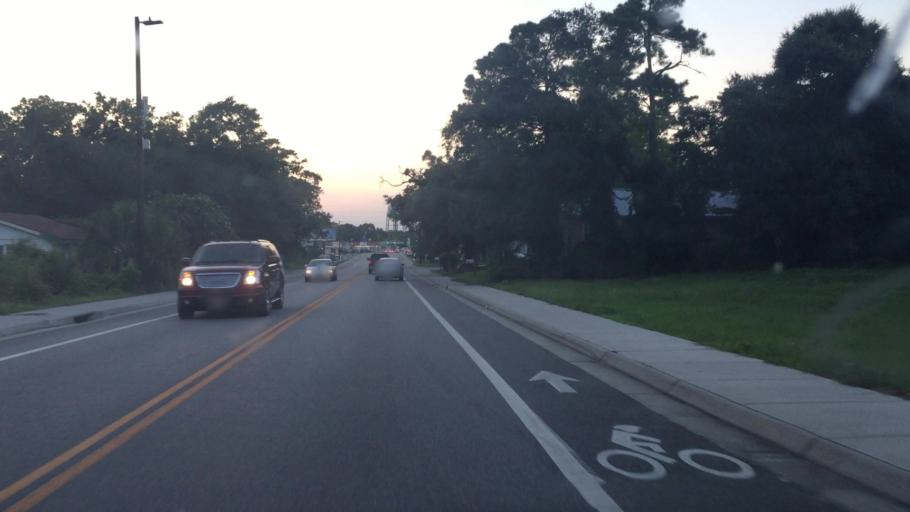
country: US
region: South Carolina
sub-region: Horry County
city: Myrtle Beach
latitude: 33.6871
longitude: -78.8937
